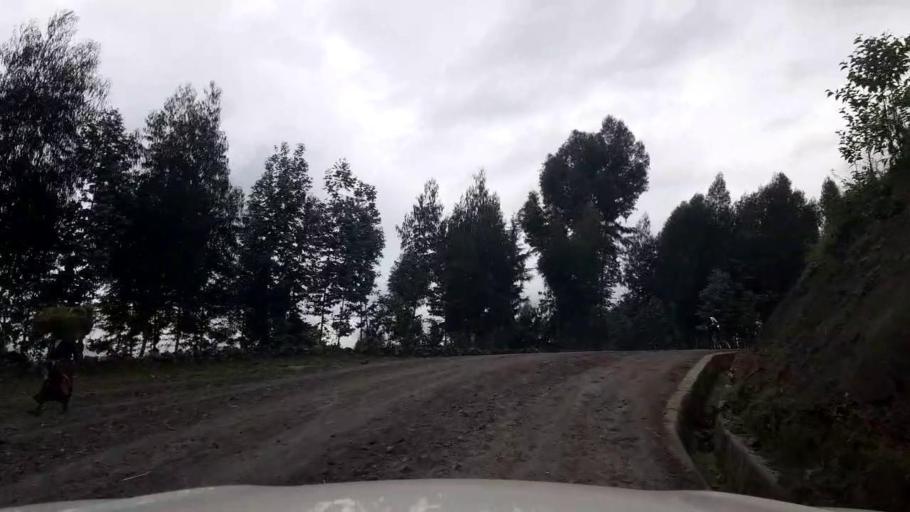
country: RW
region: Northern Province
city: Musanze
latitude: -1.5230
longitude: 29.5334
